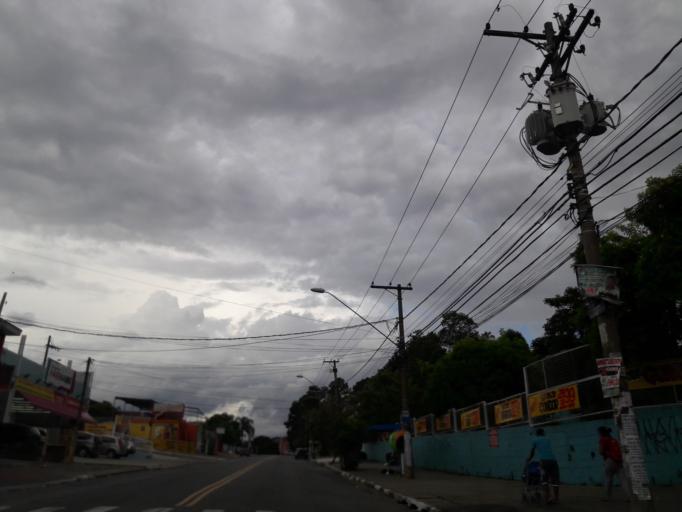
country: BR
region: Sao Paulo
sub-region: Aruja
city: Aruja
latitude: -23.4065
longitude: -46.4030
